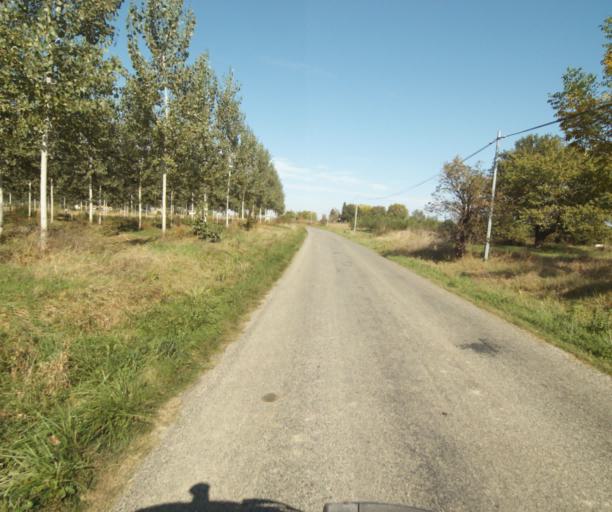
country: FR
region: Midi-Pyrenees
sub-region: Departement du Tarn-et-Garonne
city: Verdun-sur-Garonne
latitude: 43.8653
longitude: 1.2439
